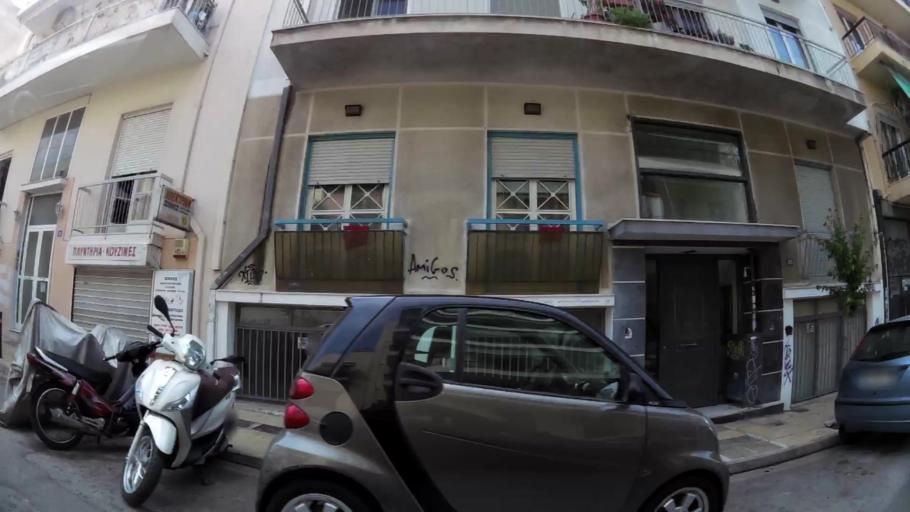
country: GR
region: Attica
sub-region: Nomarchia Athinas
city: Athens
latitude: 37.9766
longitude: 23.7157
